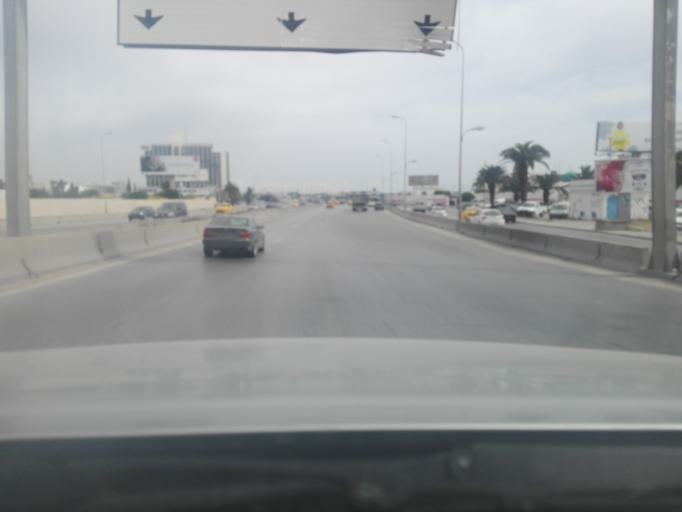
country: TN
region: Tunis
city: Tunis
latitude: 36.8025
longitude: 10.1886
